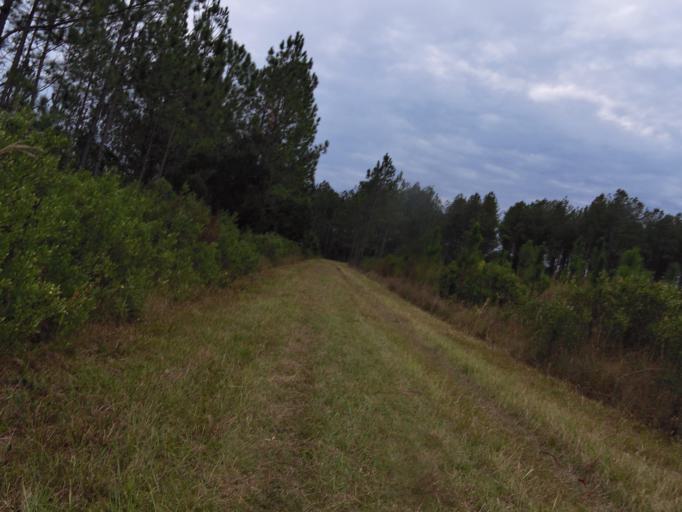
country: US
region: Florida
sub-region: Putnam County
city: Palatka
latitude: 29.6829
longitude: -81.7381
